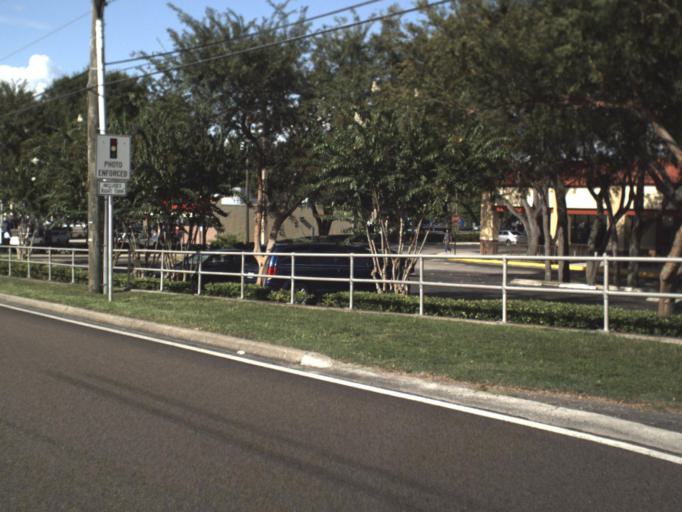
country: US
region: Florida
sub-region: Hillsborough County
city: Temple Terrace
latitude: 28.0530
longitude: -82.3935
